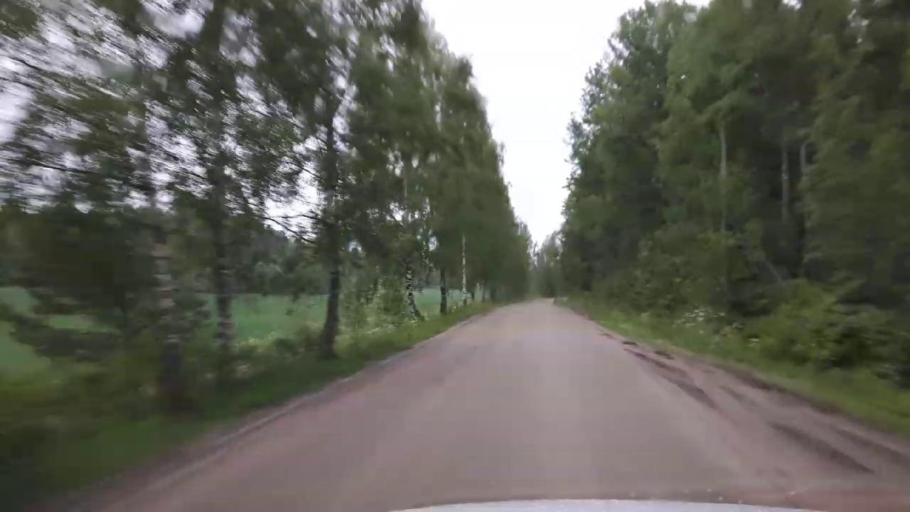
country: SE
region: Soedermanland
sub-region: Eskilstuna Kommun
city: Kvicksund
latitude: 59.4145
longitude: 16.2434
